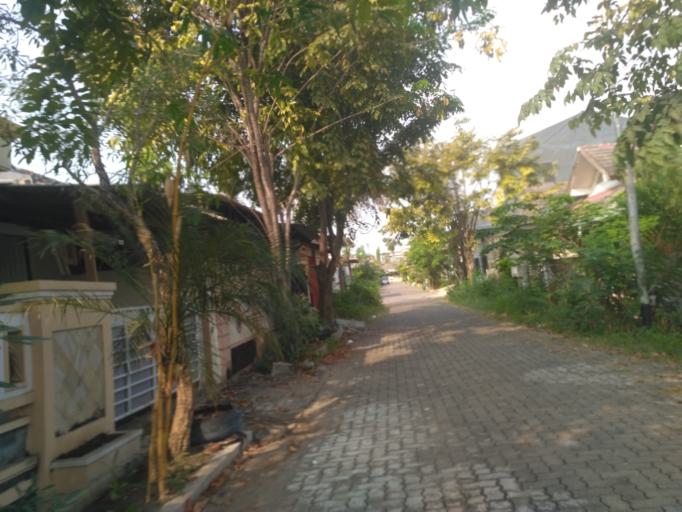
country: ID
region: Central Java
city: Semarang
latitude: -6.9667
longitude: 110.3842
